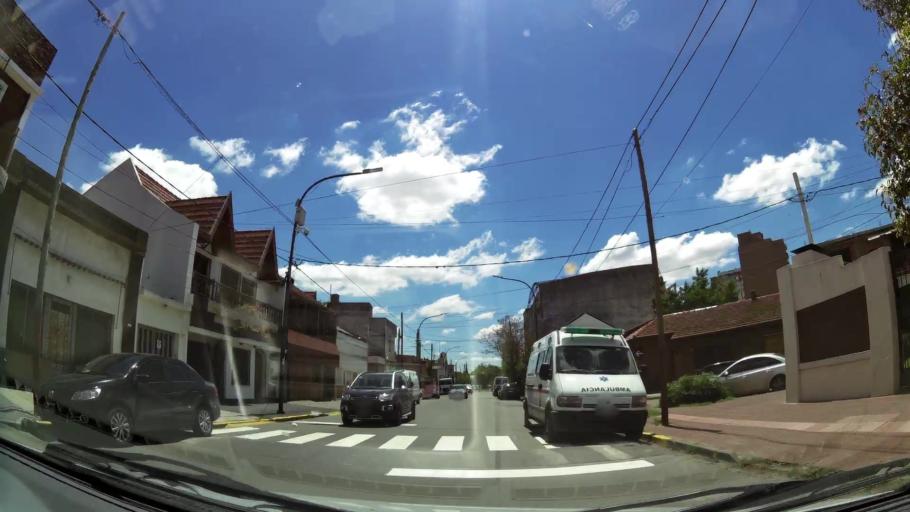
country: AR
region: Buenos Aires
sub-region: Partido de Lanus
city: Lanus
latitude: -34.7291
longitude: -58.3975
